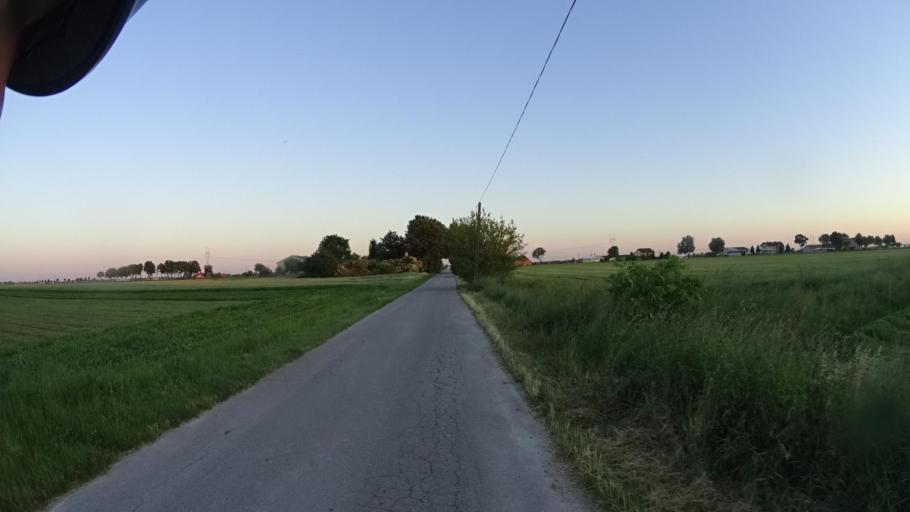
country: PL
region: Masovian Voivodeship
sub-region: Powiat warszawski zachodni
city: Blonie
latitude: 52.2398
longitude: 20.6585
